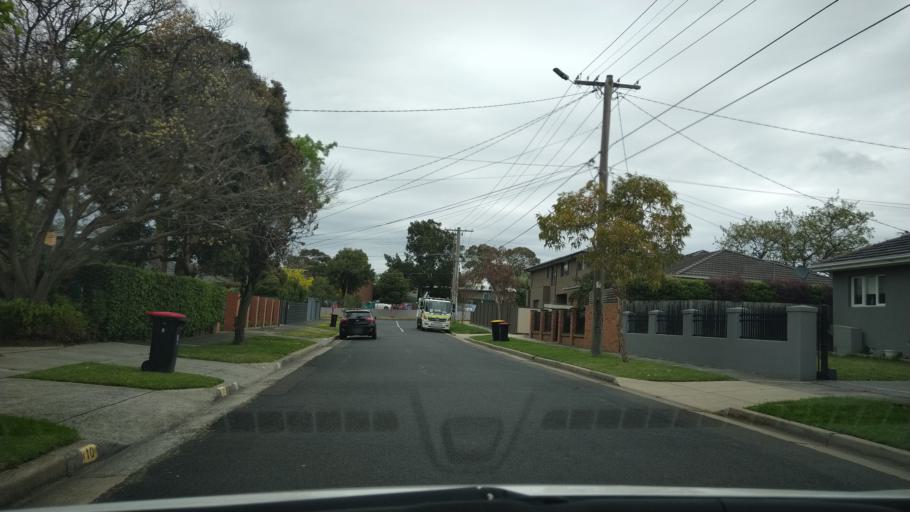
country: AU
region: Victoria
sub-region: Kingston
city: Mentone
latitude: -37.9642
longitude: 145.0688
